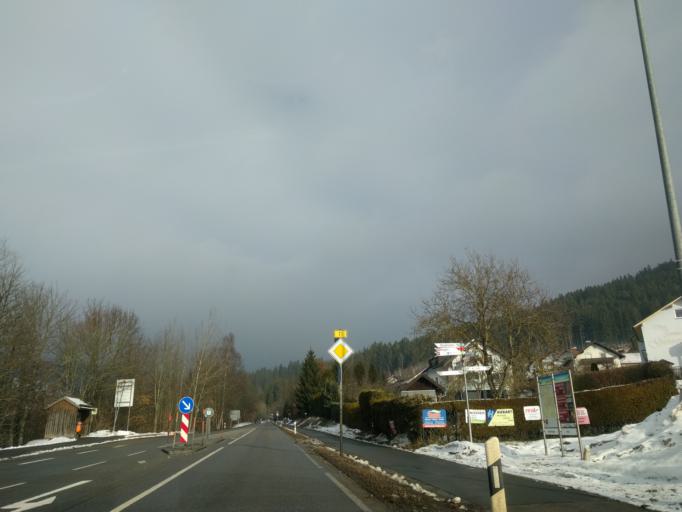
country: DE
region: Bavaria
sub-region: Lower Bavaria
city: Zwiesel
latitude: 49.0358
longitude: 13.2335
